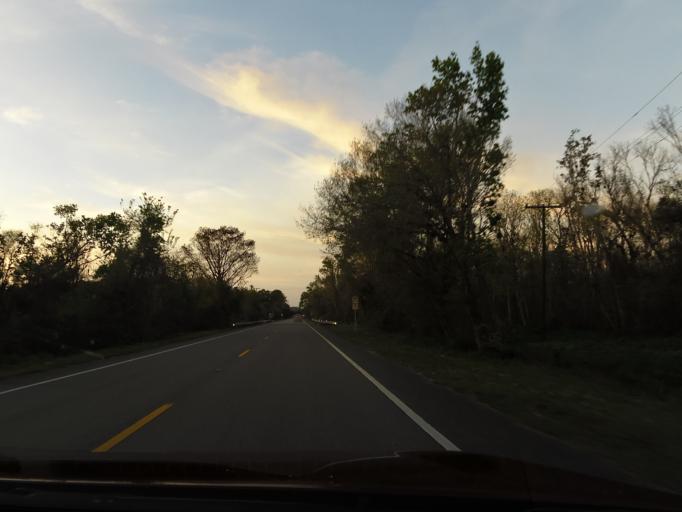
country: US
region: Florida
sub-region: Volusia County
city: De Leon Springs
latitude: 29.1657
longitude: -81.2984
